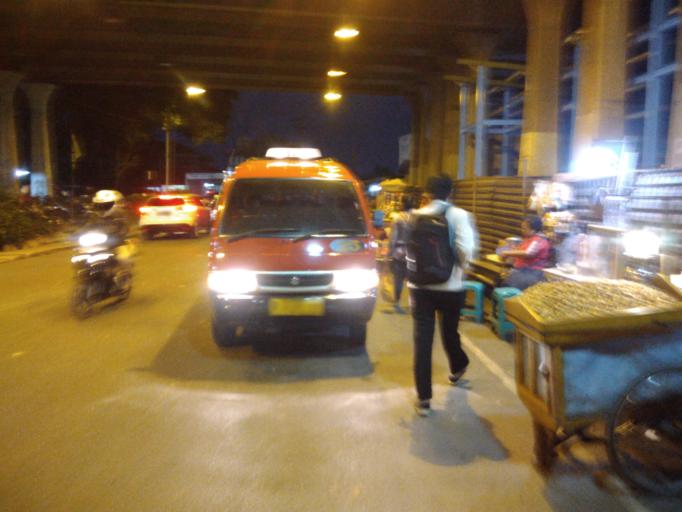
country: ID
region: West Java
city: Bekasi
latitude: -6.2189
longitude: 106.9527
